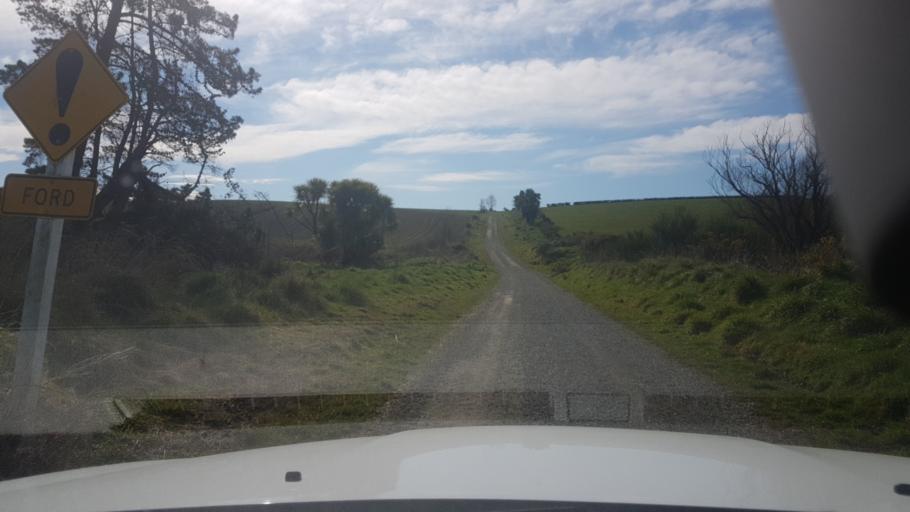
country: NZ
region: Canterbury
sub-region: Timaru District
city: Pleasant Point
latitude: -44.2021
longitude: 171.1868
